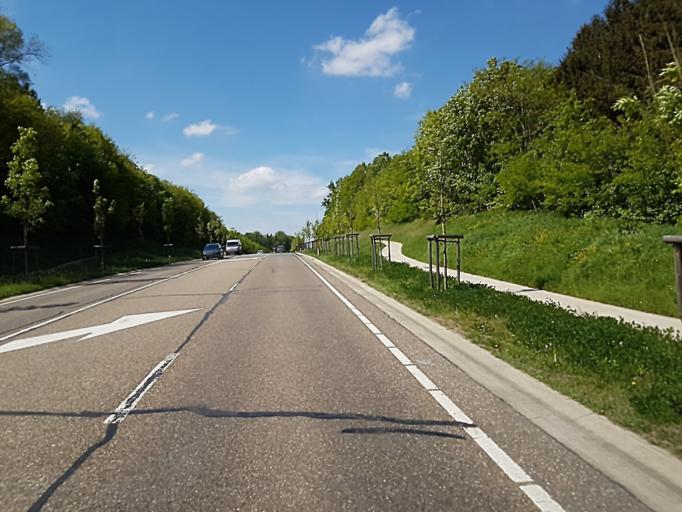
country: BE
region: Flanders
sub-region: Provincie Vlaams-Brabant
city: Lubbeek
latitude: 50.9162
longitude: 4.8587
